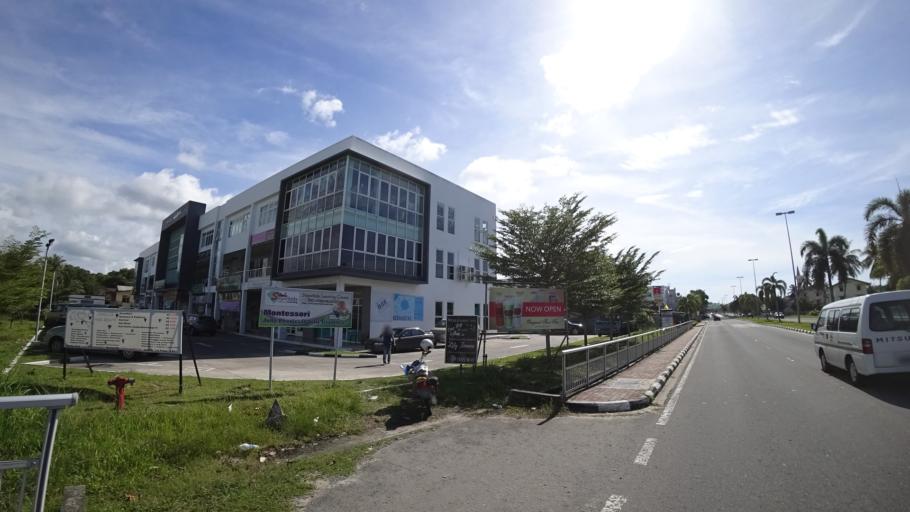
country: BN
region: Brunei and Muara
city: Bandar Seri Begawan
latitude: 4.9449
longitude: 114.9487
